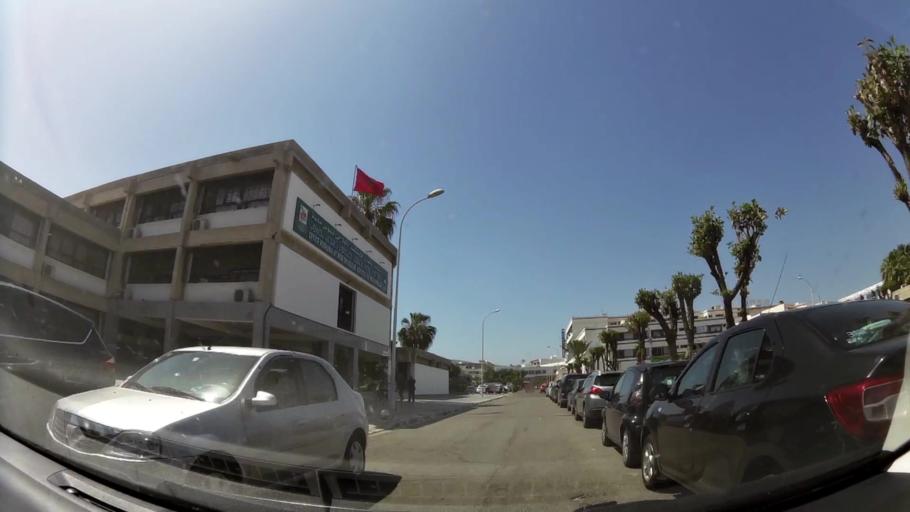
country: MA
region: Souss-Massa-Draa
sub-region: Agadir-Ida-ou-Tnan
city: Agadir
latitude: 30.4214
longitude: -9.6020
